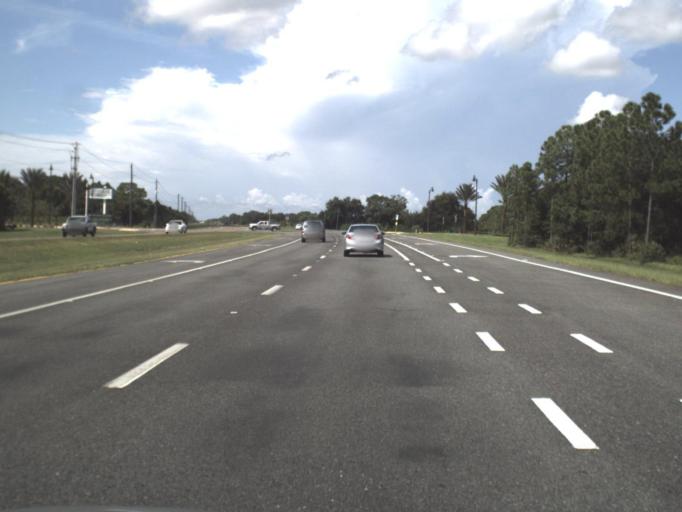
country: US
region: Florida
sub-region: Sarasota County
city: Plantation
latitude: 27.0493
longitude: -82.3190
